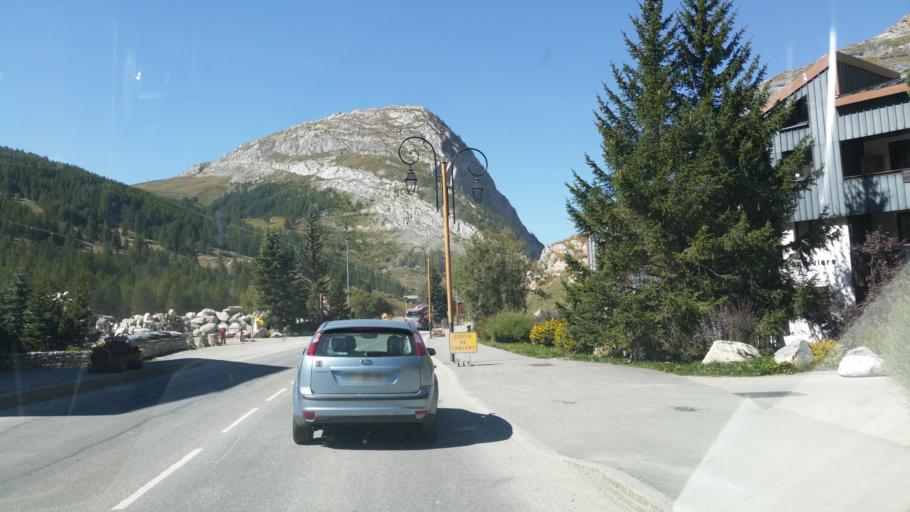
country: FR
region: Rhone-Alpes
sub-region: Departement de la Savoie
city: Val-d'Isere
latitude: 45.4544
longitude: 6.9710
